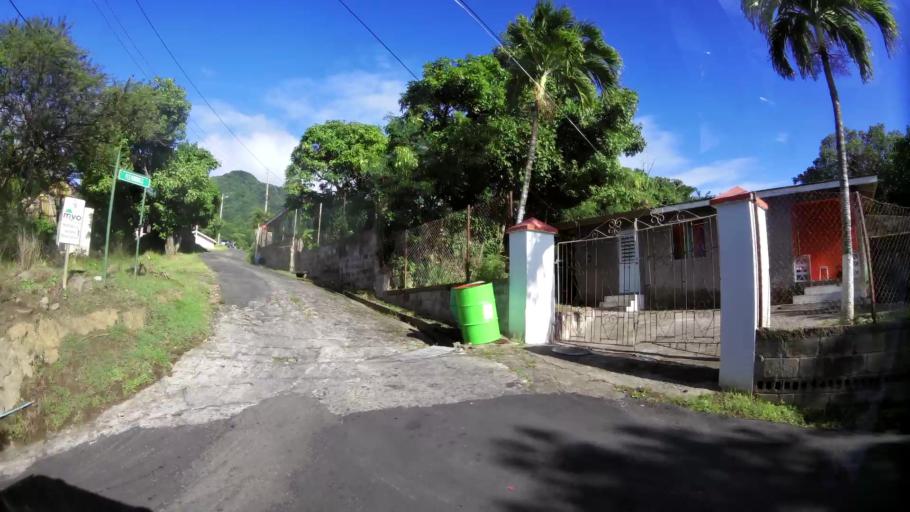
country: MS
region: Saint Peter
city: Saint Peters
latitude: 16.7473
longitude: -62.2189
